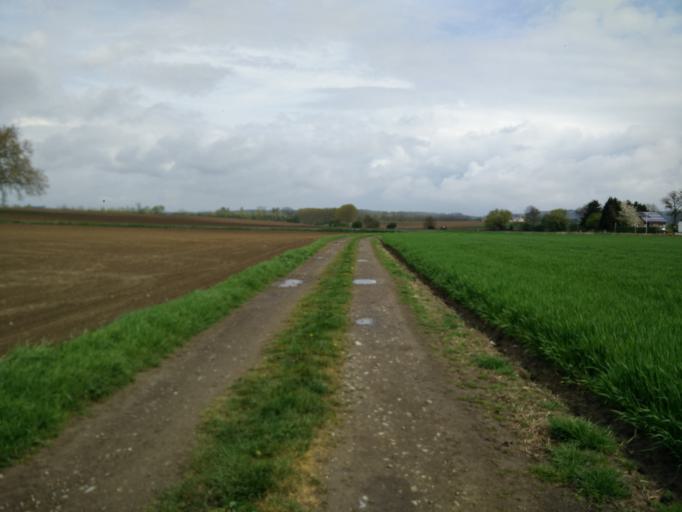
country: BE
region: Wallonia
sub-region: Province de Liege
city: Dalhem
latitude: 50.7365
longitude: 5.7512
